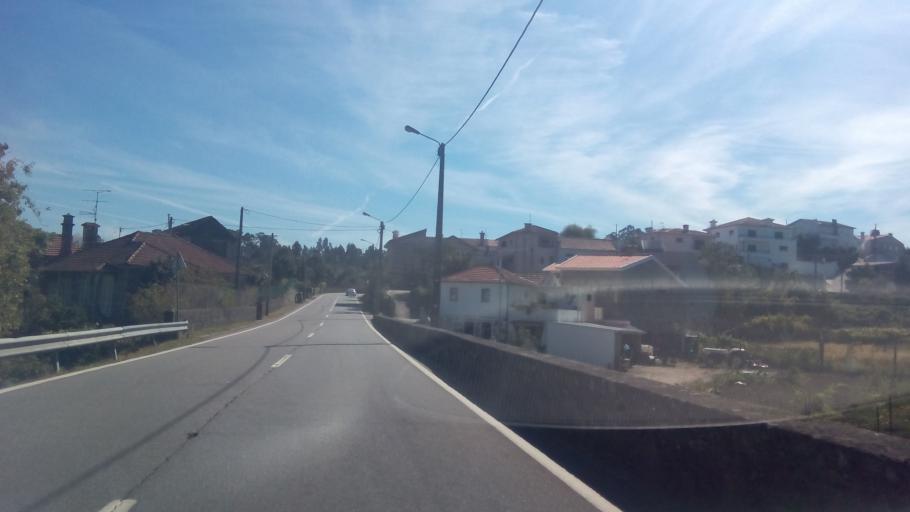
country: PT
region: Porto
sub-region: Paredes
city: Baltar
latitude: 41.1853
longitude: -8.3894
